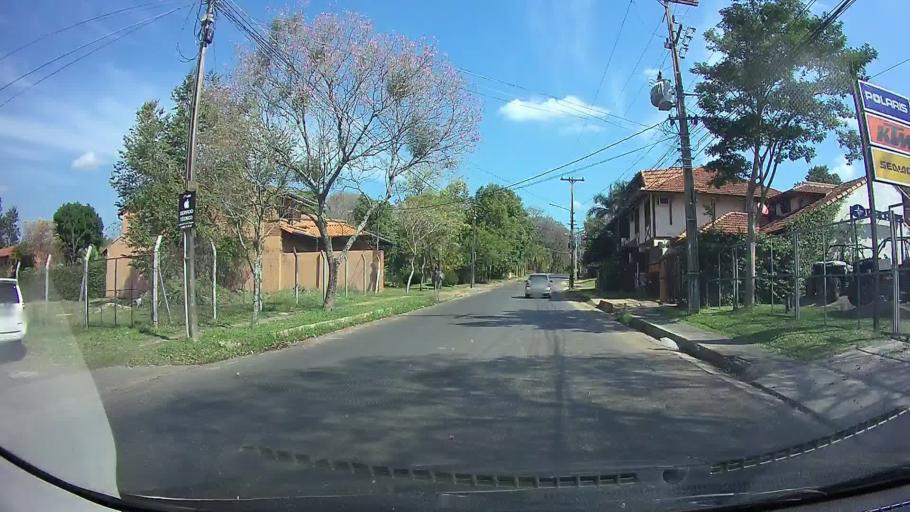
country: PY
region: Central
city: Fernando de la Mora
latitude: -25.2803
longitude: -57.5523
